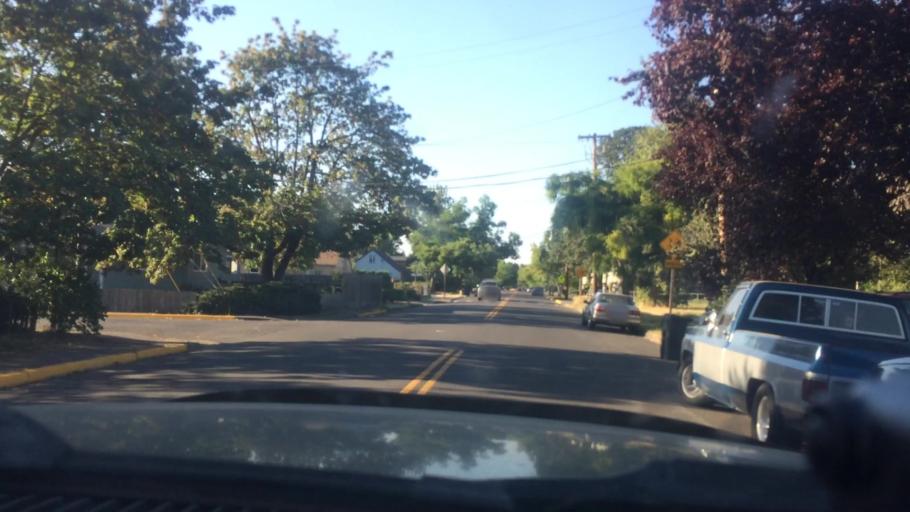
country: US
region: Oregon
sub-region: Lane County
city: Eugene
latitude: 44.0414
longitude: -123.1125
